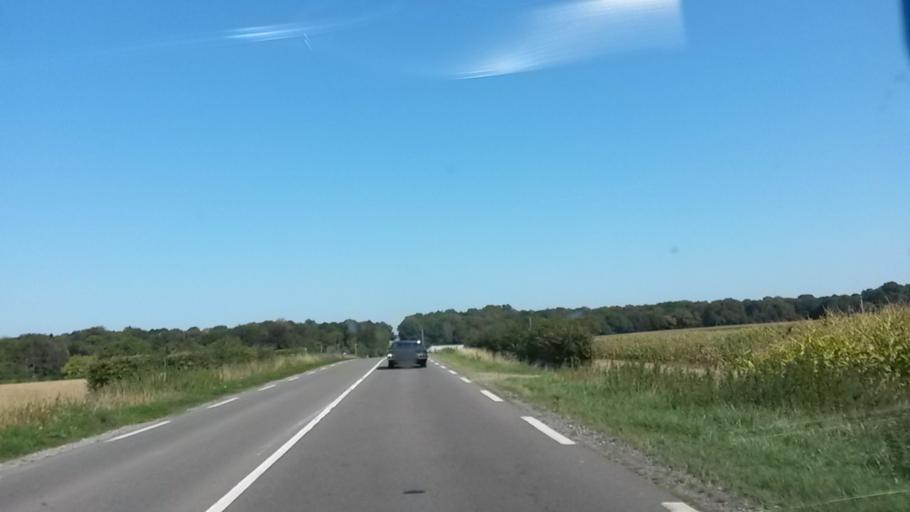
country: FR
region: Nord-Pas-de-Calais
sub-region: Departement du Nord
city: Hautmont
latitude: 50.1884
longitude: 3.9516
